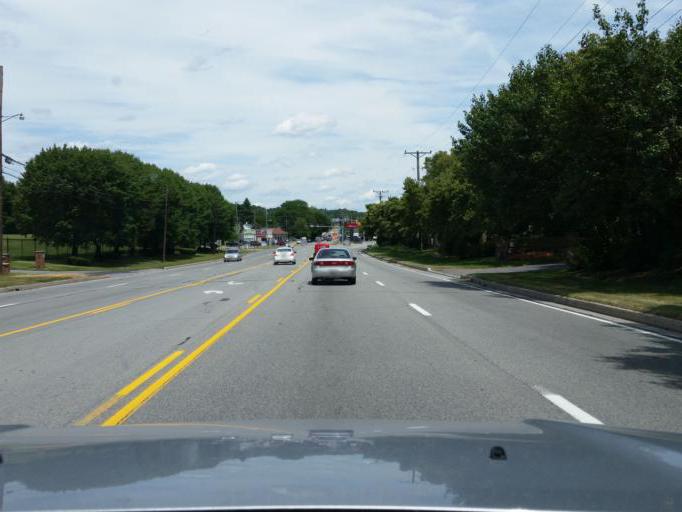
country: US
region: Pennsylvania
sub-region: Blair County
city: Lakemont
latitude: 40.4951
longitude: -78.3951
